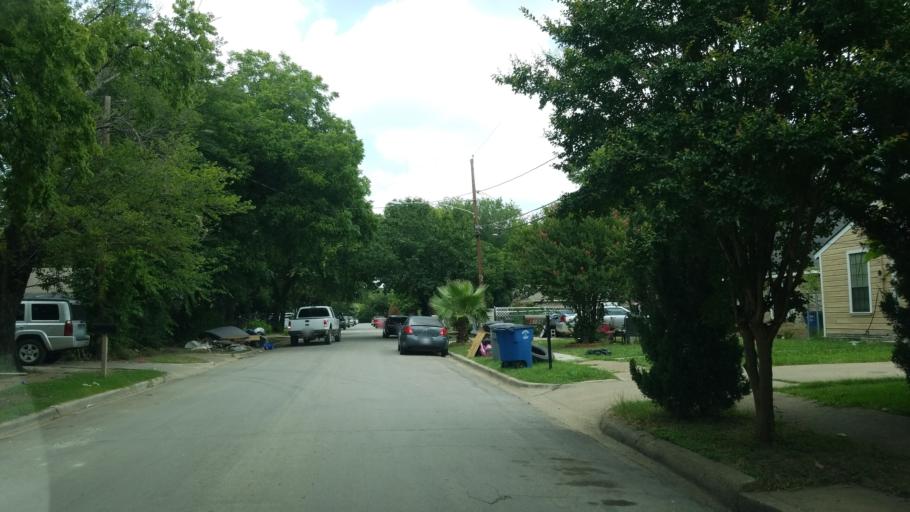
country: US
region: Texas
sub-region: Dallas County
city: Irving
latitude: 32.7919
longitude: -96.8981
